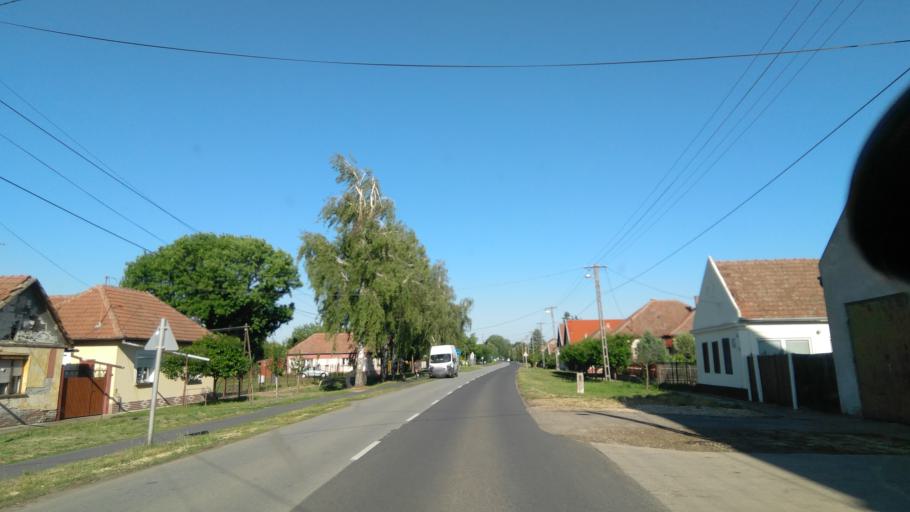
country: HU
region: Bekes
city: Elek
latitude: 46.5322
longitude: 21.2403
